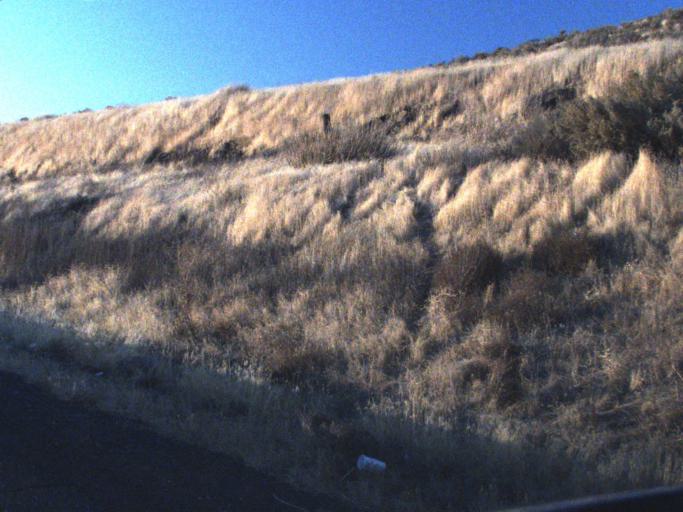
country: US
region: Washington
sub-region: Adams County
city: Ritzville
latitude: 46.9708
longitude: -118.6500
